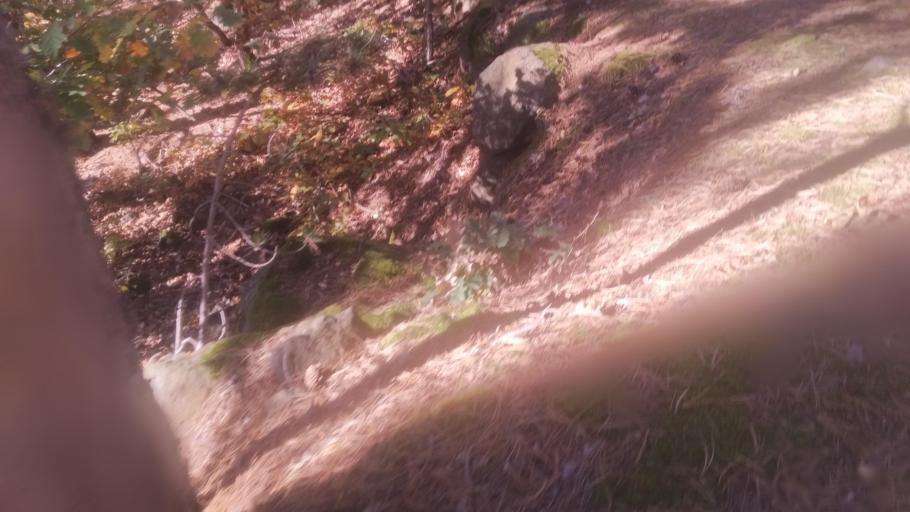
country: HU
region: Pest
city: Pilisborosjeno
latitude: 47.6190
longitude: 19.0111
